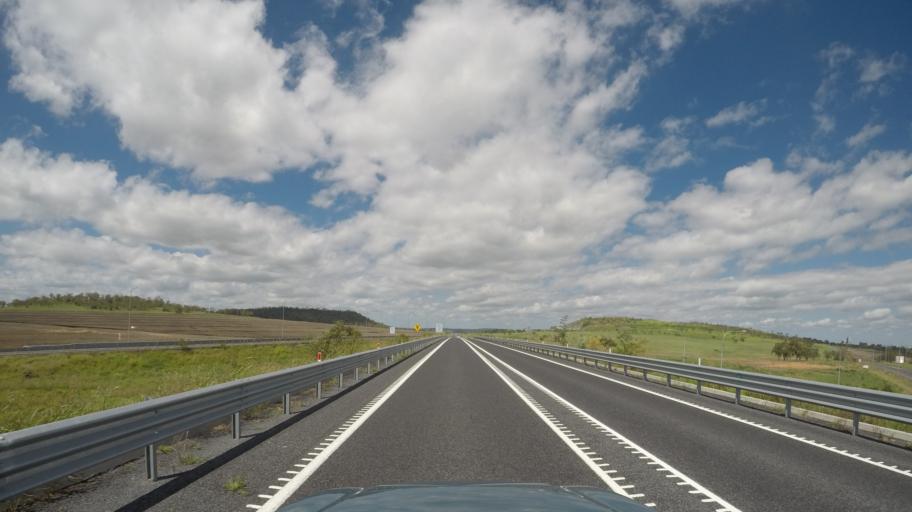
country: AU
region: Queensland
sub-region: Toowoomba
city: Westbrook
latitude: -27.5476
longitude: 151.8333
